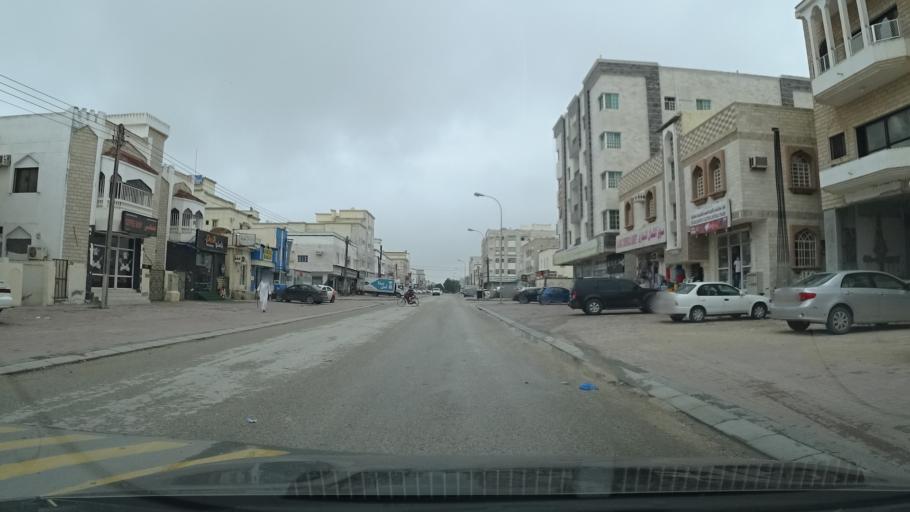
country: OM
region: Zufar
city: Salalah
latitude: 17.0172
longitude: 54.0677
